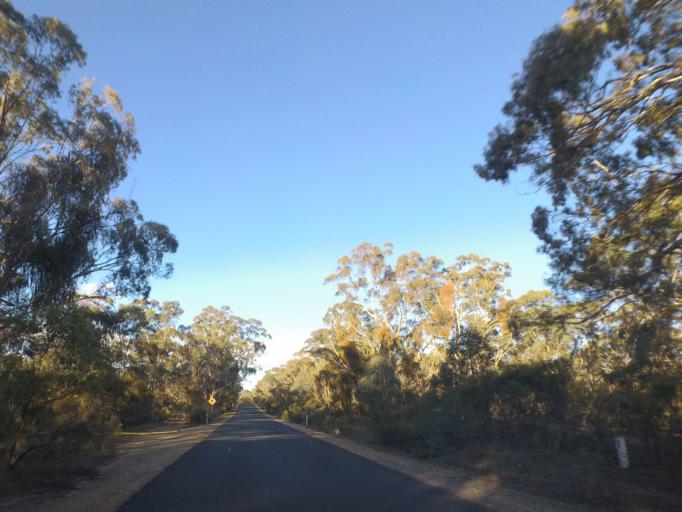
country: AU
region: Victoria
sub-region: Mount Alexander
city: Castlemaine
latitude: -37.1562
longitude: 144.2235
